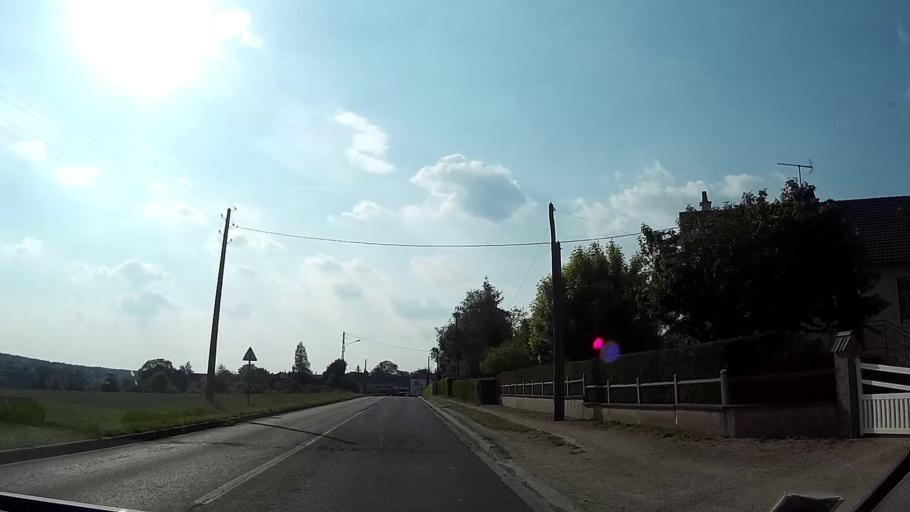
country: FR
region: Centre
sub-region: Departement du Loir-et-Cher
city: Saint-Sulpice-de-Pommeray
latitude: 47.6067
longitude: 1.2762
